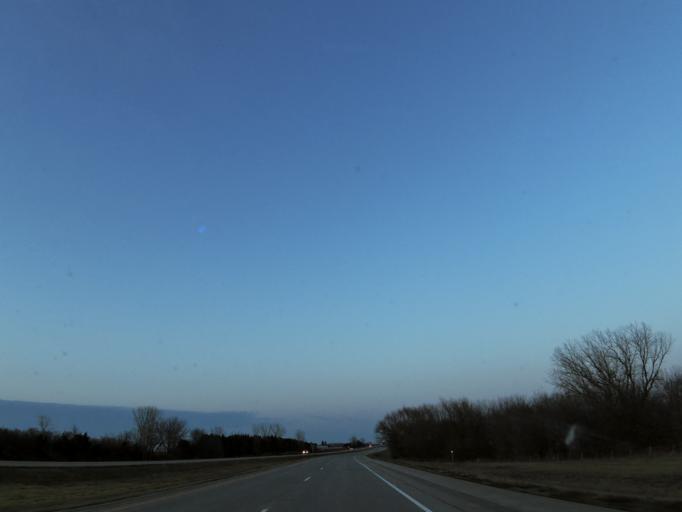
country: US
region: Minnesota
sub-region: Mower County
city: Grand Meadow
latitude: 43.6940
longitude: -92.7250
